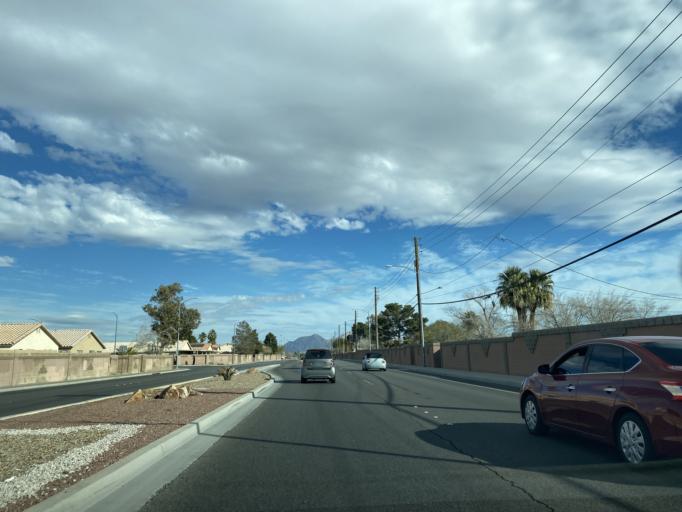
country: US
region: Nevada
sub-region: Clark County
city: Las Vegas
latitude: 36.1884
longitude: -115.1686
